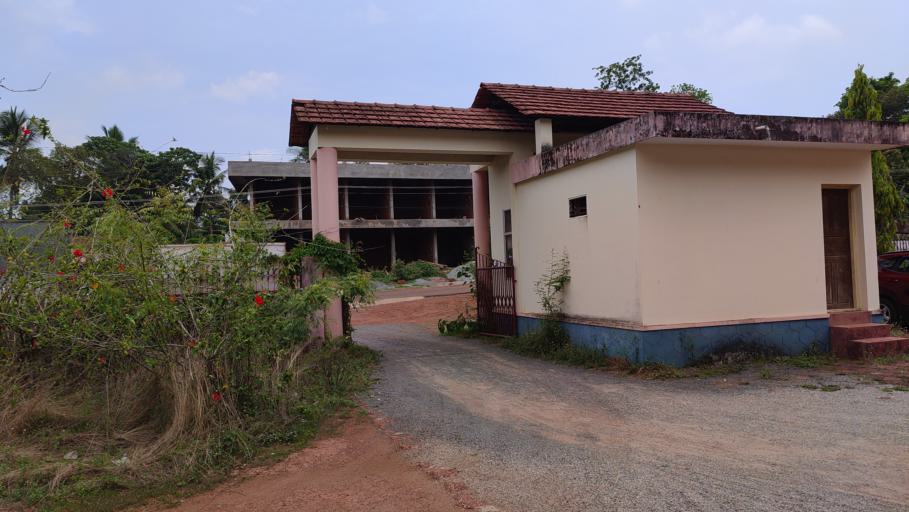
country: IN
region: Kerala
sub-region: Kasaragod District
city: Kannangad
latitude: 12.3210
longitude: 75.1063
